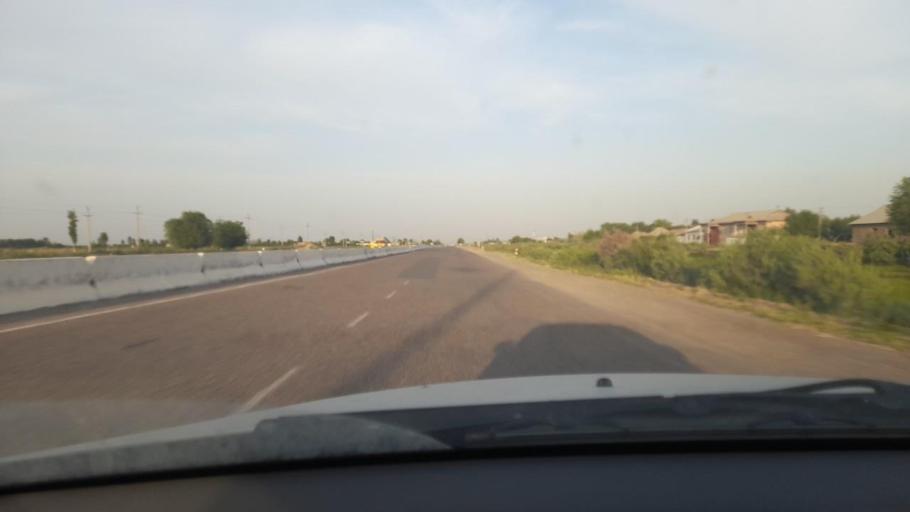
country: UZ
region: Sirdaryo
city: Guliston
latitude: 40.4955
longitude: 68.6356
